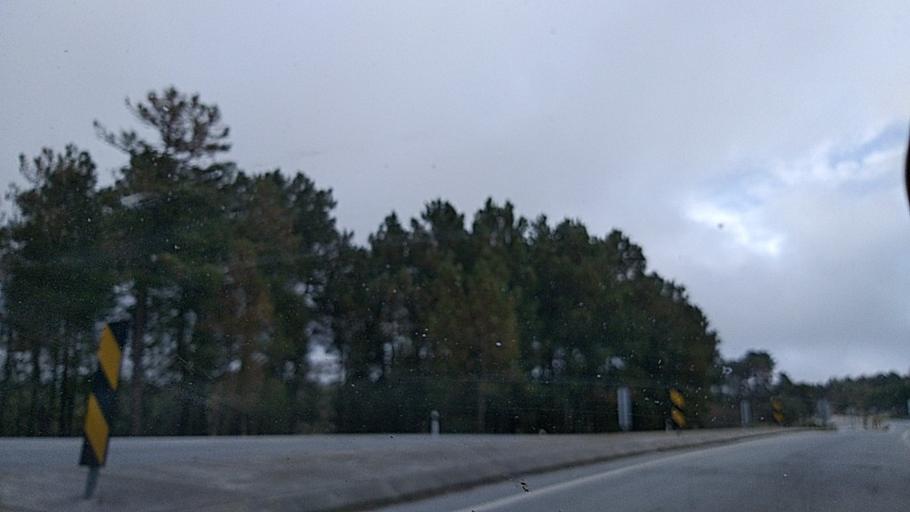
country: PT
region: Guarda
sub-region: Aguiar da Beira
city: Aguiar da Beira
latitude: 40.7310
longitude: -7.4953
